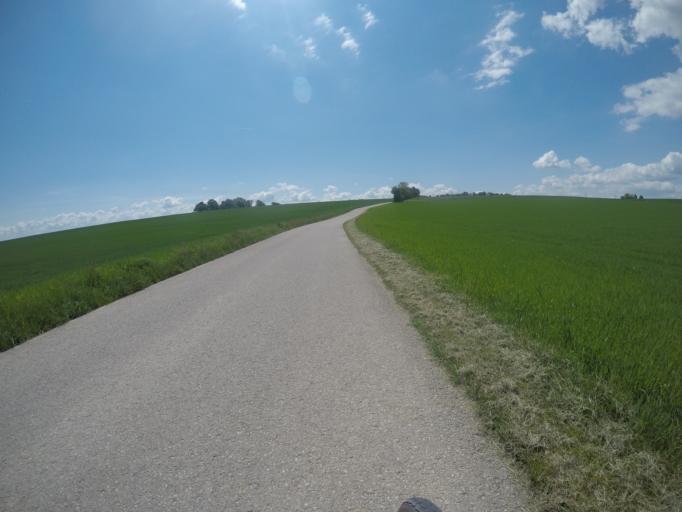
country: DE
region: Baden-Wuerttemberg
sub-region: Regierungsbezirk Stuttgart
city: Oberjettingen
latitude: 48.5823
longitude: 8.8002
